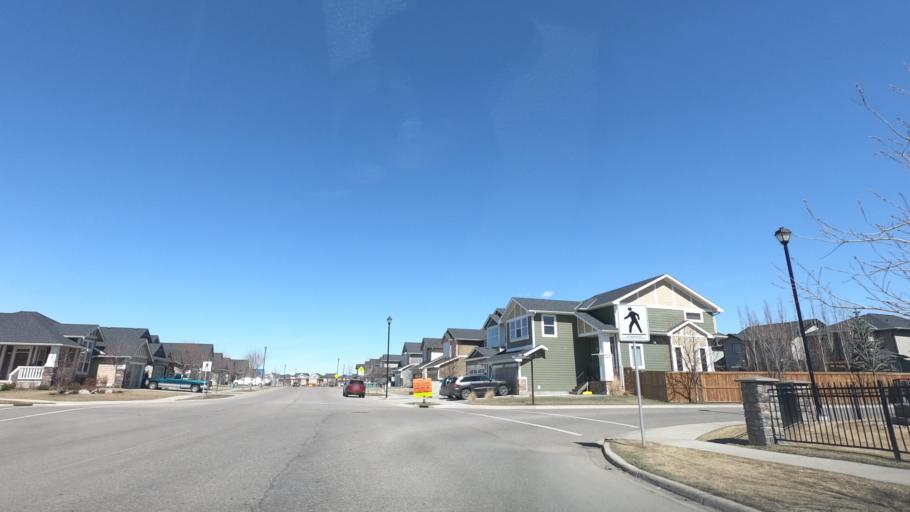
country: CA
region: Alberta
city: Airdrie
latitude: 51.3011
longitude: -114.0331
